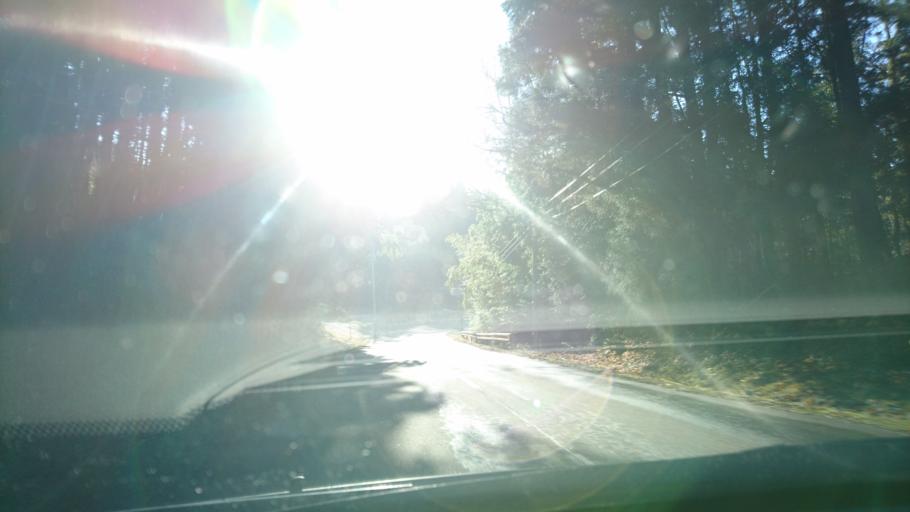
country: JP
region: Iwate
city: Ichinoseki
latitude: 38.8673
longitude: 141.2964
